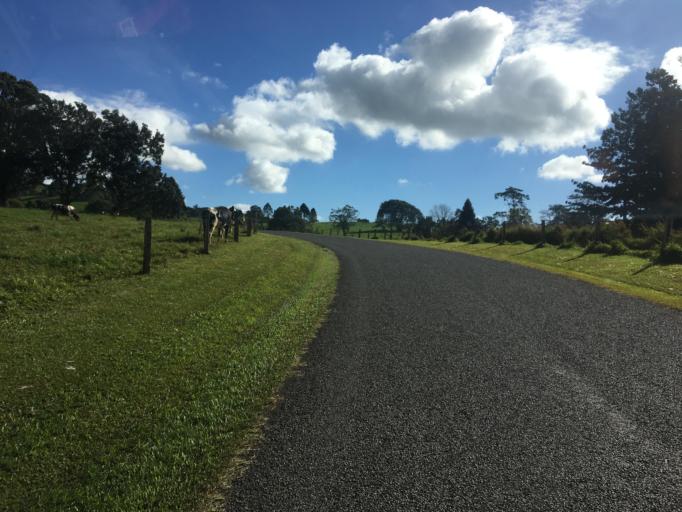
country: AU
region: Queensland
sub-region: Tablelands
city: Ravenshoe
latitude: -17.5265
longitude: 145.6125
